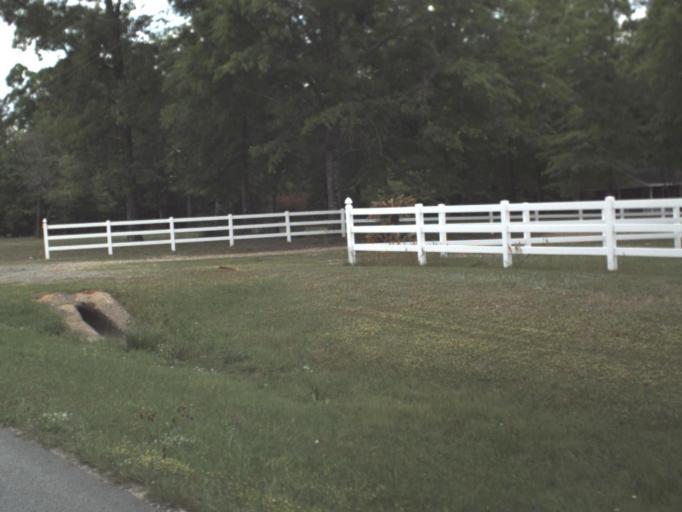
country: US
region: Alabama
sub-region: Escambia County
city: Atmore
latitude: 30.9224
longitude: -87.4803
